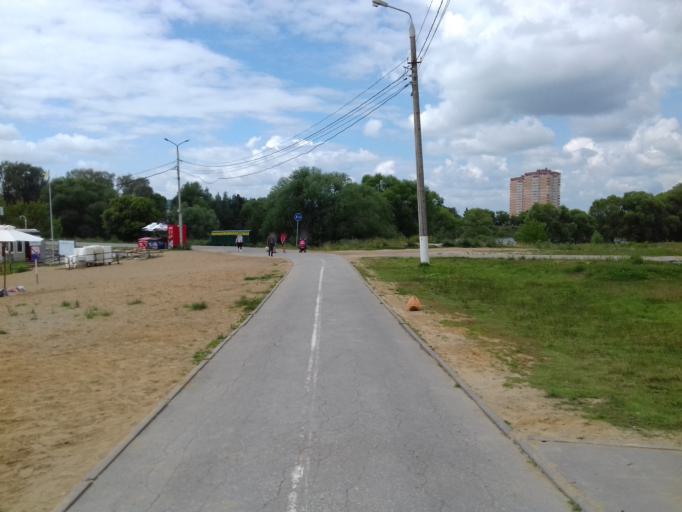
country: RU
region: Tula
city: Tula
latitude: 54.1833
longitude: 37.5807
